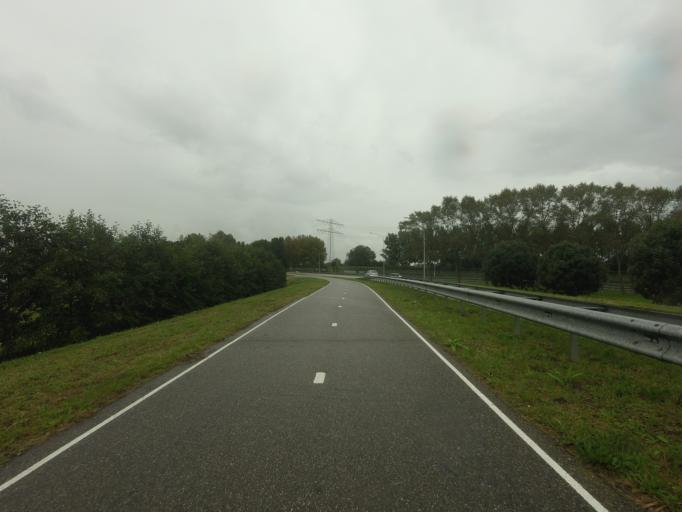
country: NL
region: South Holland
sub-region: Gemeente Papendrecht
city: Papendrecht
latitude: 51.8447
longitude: 4.6957
